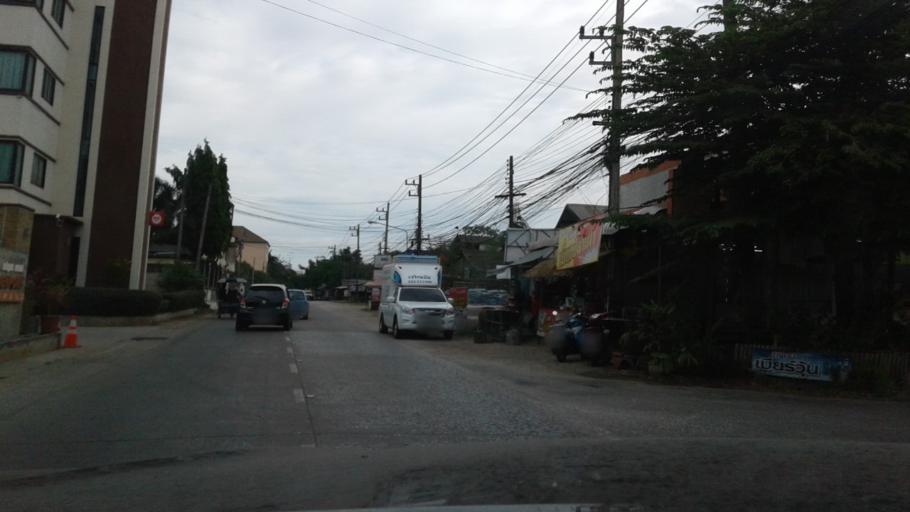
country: TH
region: Changwat Udon Thani
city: Udon Thani
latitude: 17.4002
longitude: 102.7723
